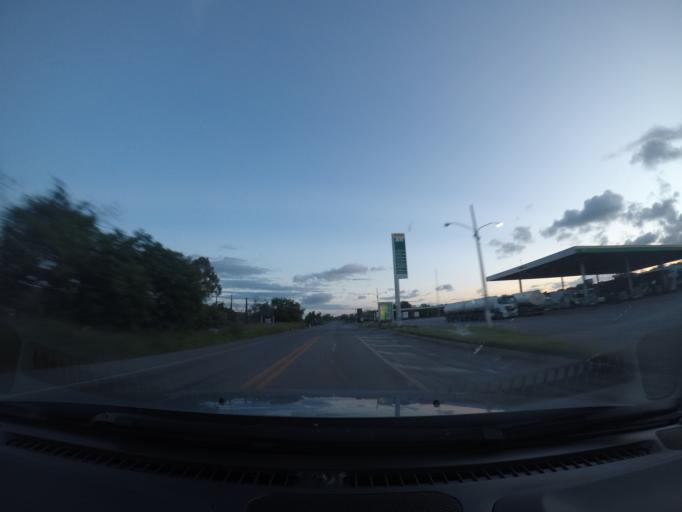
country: BR
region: Bahia
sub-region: Seabra
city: Seabra
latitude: -12.4494
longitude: -41.7511
